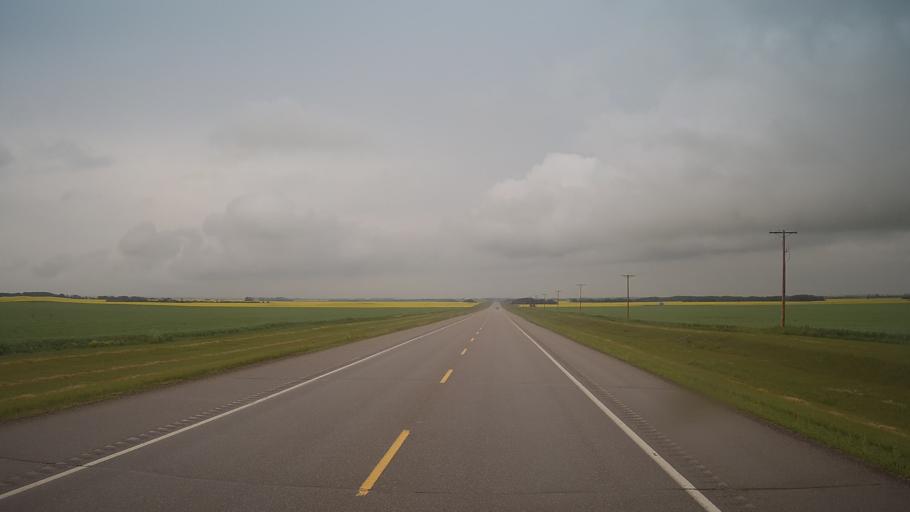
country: CA
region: Saskatchewan
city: Wilkie
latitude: 52.4205
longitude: -108.8953
